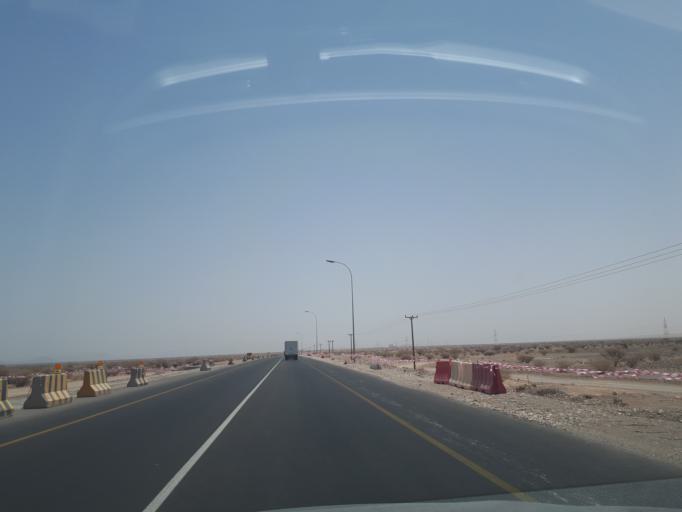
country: OM
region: Ash Sharqiyah
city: Badiyah
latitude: 22.4246
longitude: 59.0414
